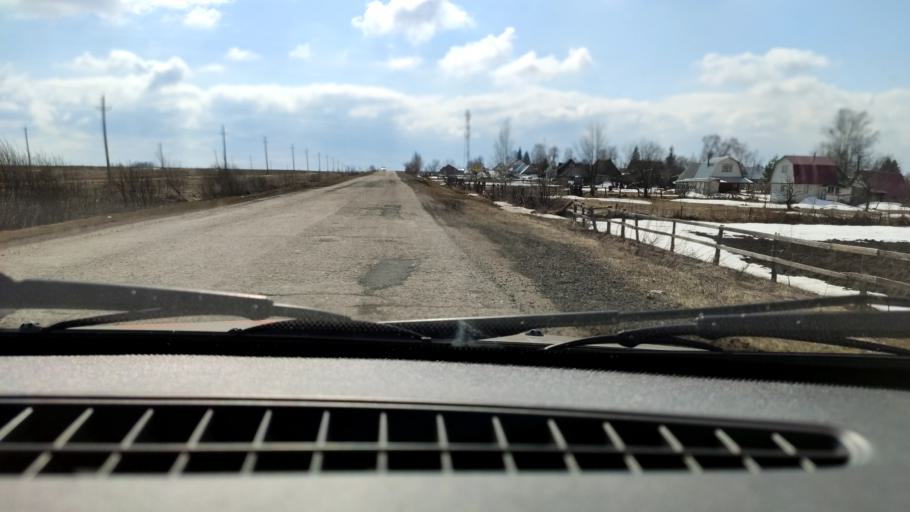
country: RU
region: Bashkortostan
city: Kudeyevskiy
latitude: 54.8498
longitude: 56.7954
